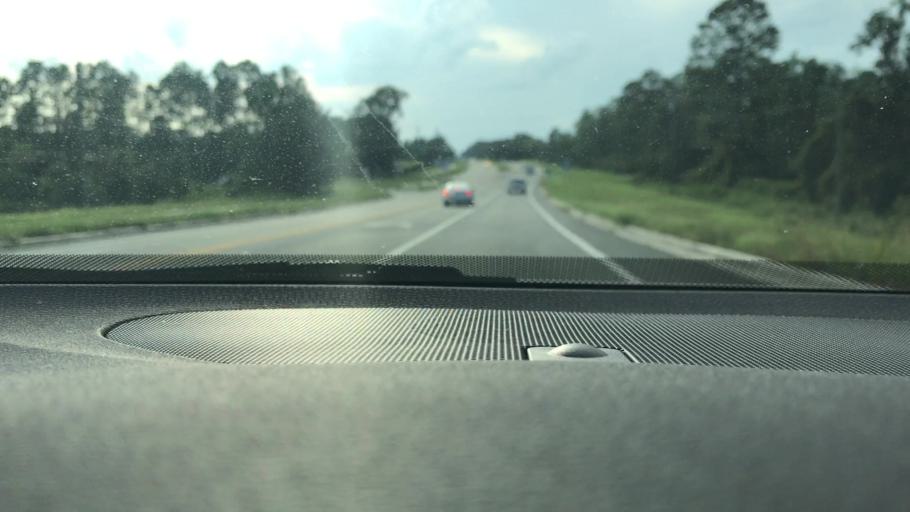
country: US
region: Florida
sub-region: Volusia County
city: Lake Helen
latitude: 28.9847
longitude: -81.2502
